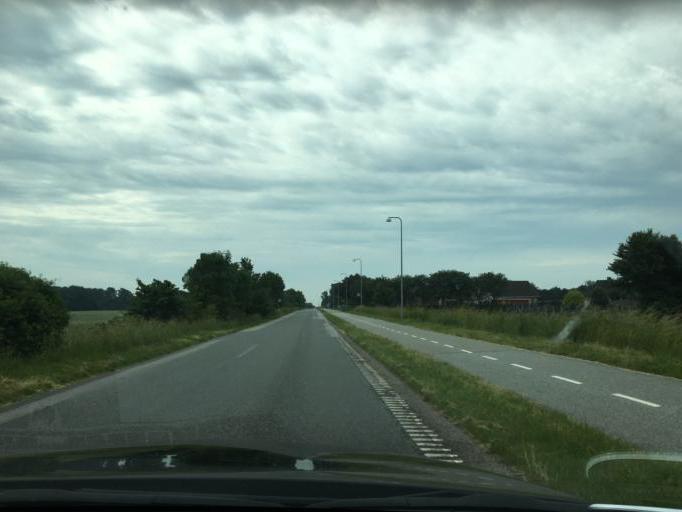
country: DK
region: South Denmark
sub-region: Kolding Kommune
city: Kolding
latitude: 55.5774
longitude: 9.4919
